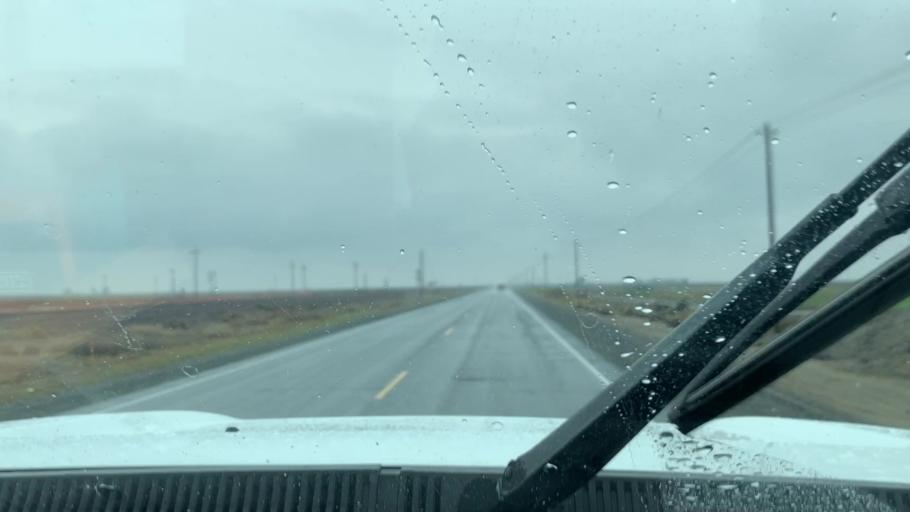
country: US
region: California
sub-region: Tulare County
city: Alpaugh
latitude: 35.9473
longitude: -119.4461
